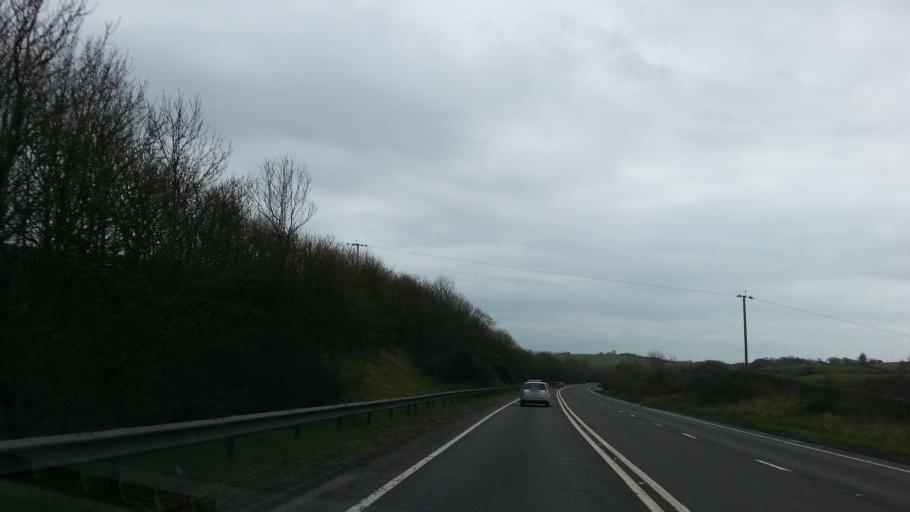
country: GB
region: England
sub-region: Devon
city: Appledore
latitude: 51.0350
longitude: -4.1571
